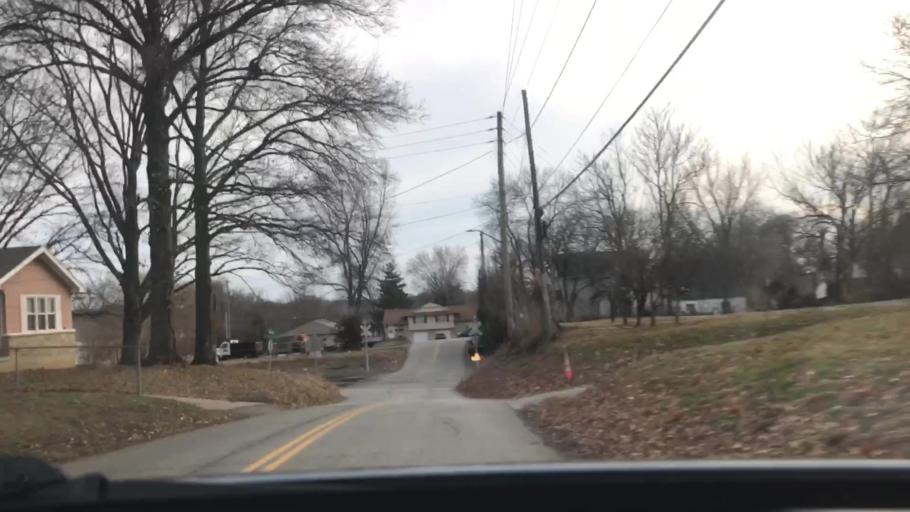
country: US
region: Missouri
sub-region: Jackson County
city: Independence
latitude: 39.0838
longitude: -94.4390
